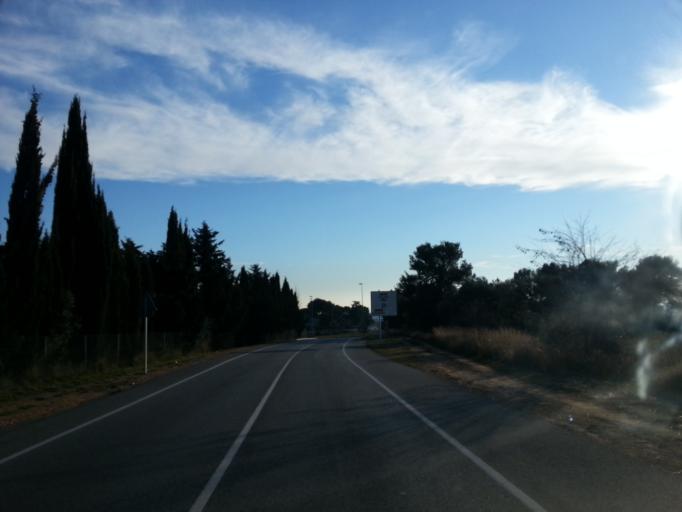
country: ES
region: Catalonia
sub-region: Provincia de Barcelona
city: Matadepera
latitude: 41.5933
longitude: 2.0198
